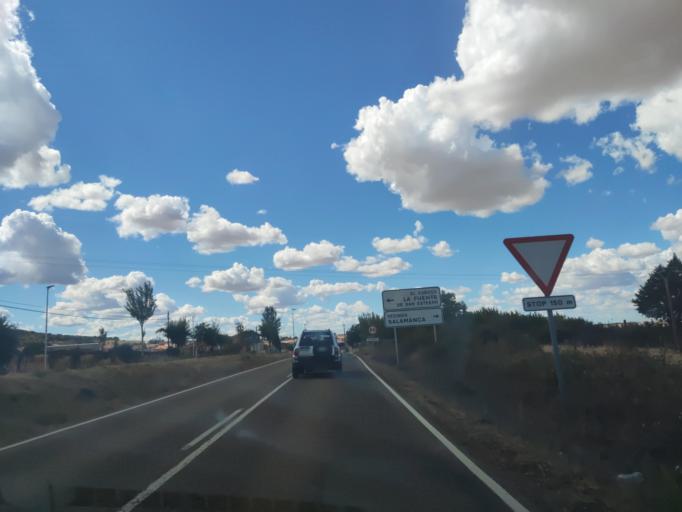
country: ES
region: Castille and Leon
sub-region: Provincia de Salamanca
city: Tamames
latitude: 40.6542
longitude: -6.0984
